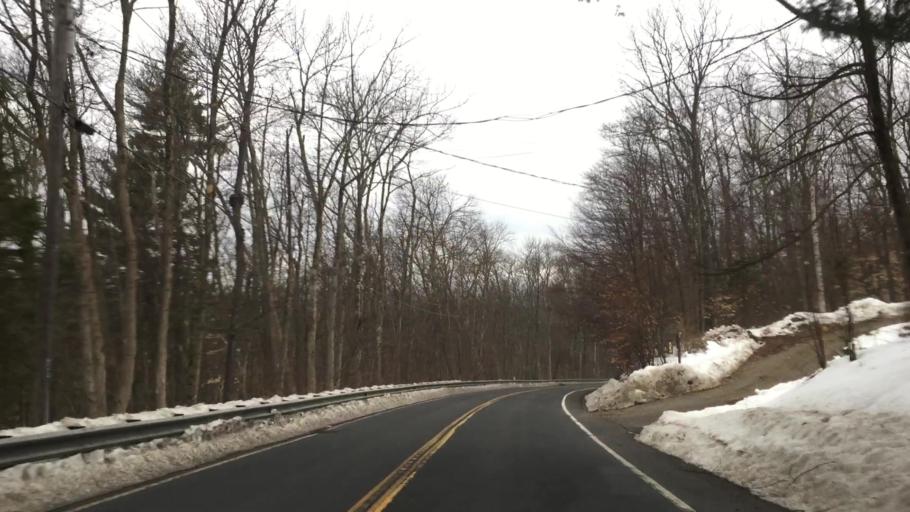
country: US
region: Massachusetts
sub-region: Berkshire County
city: Hinsdale
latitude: 42.4152
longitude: -73.0680
